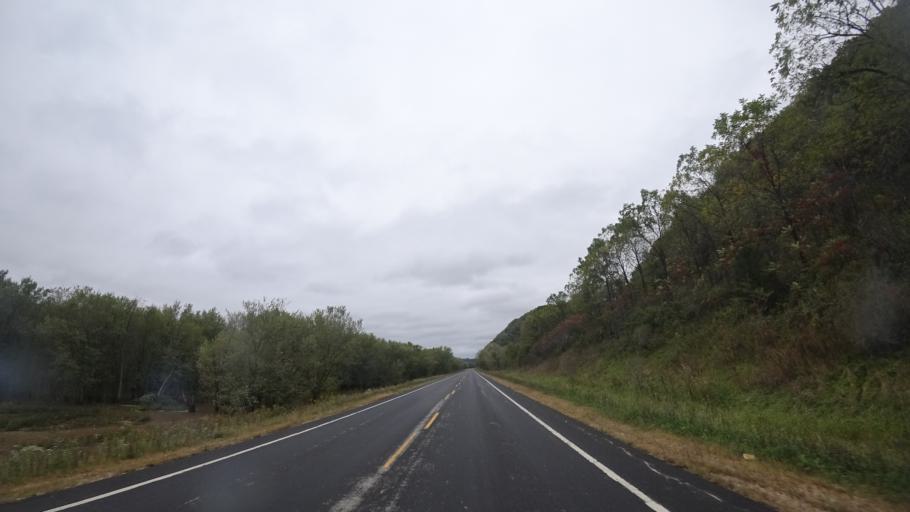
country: US
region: Wisconsin
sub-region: Grant County
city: Boscobel
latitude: 43.1878
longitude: -90.6687
